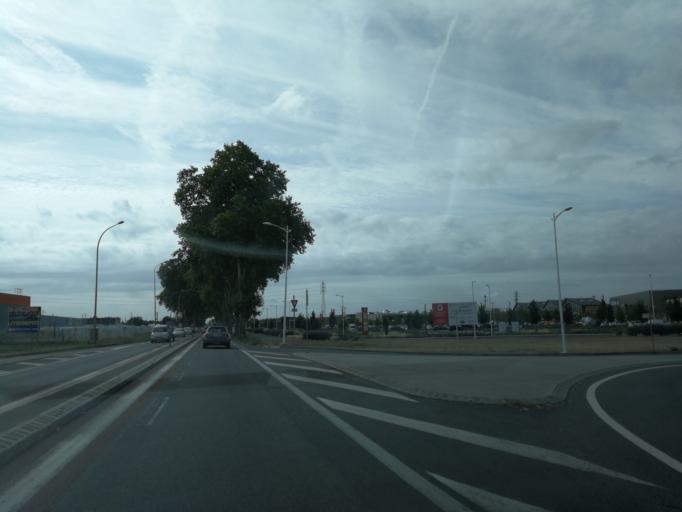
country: FR
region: Midi-Pyrenees
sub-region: Departement de la Haute-Garonne
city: Saint-Alban
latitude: 43.6956
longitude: 1.4003
